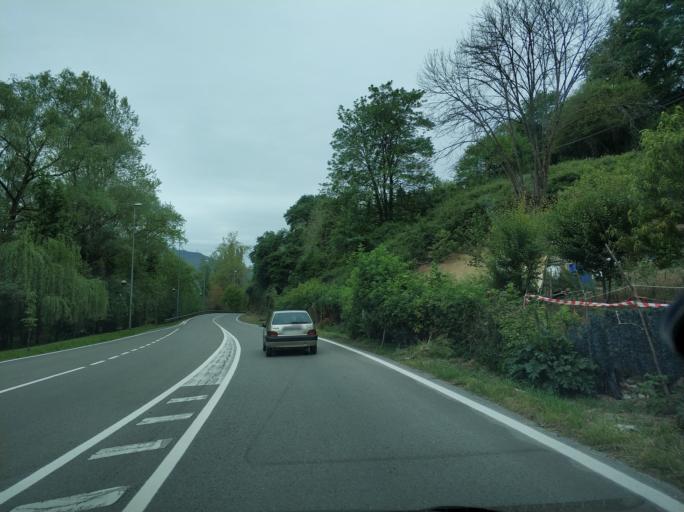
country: ES
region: Cantabria
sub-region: Provincia de Cantabria
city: Santa Maria de Cayon
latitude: 43.3204
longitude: -3.8683
